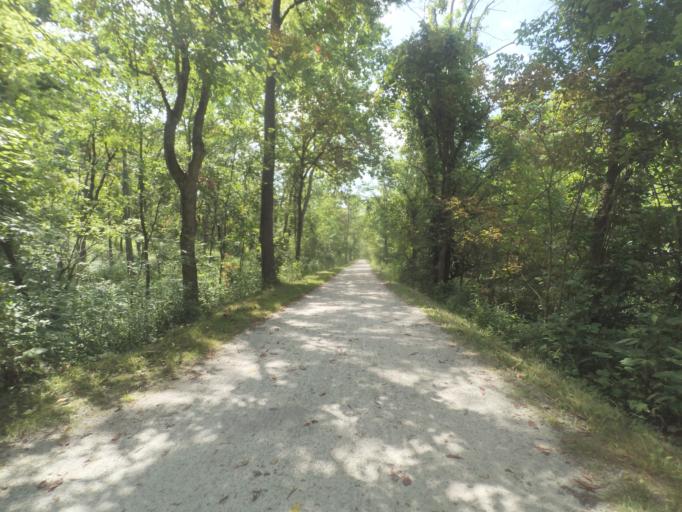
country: US
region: Ohio
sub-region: Summit County
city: Peninsula
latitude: 41.2882
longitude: -81.5639
